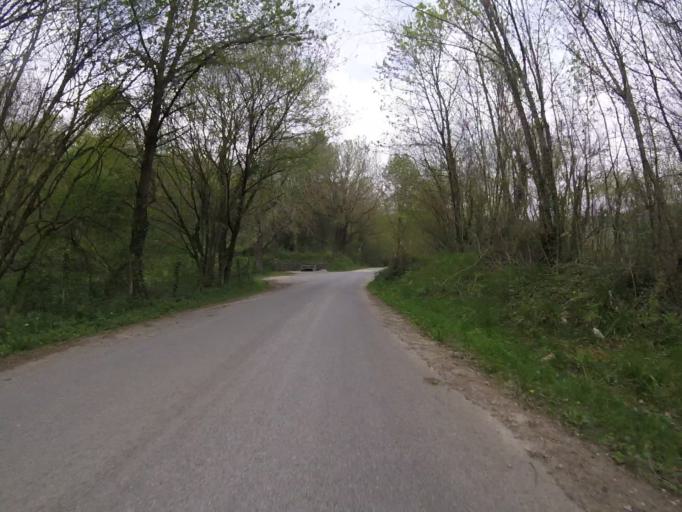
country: ES
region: Basque Country
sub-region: Provincia de Guipuzcoa
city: Asteasu
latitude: 43.2196
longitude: -2.0929
